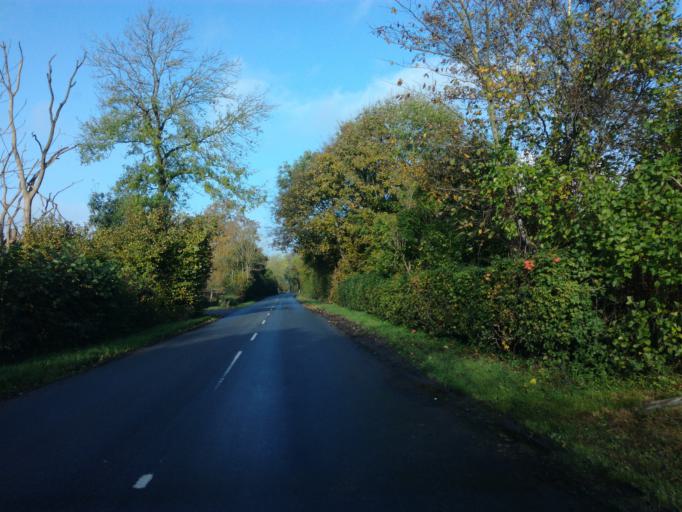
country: DK
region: South Denmark
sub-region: Vejle Kommune
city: Borkop
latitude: 55.6490
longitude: 9.6614
